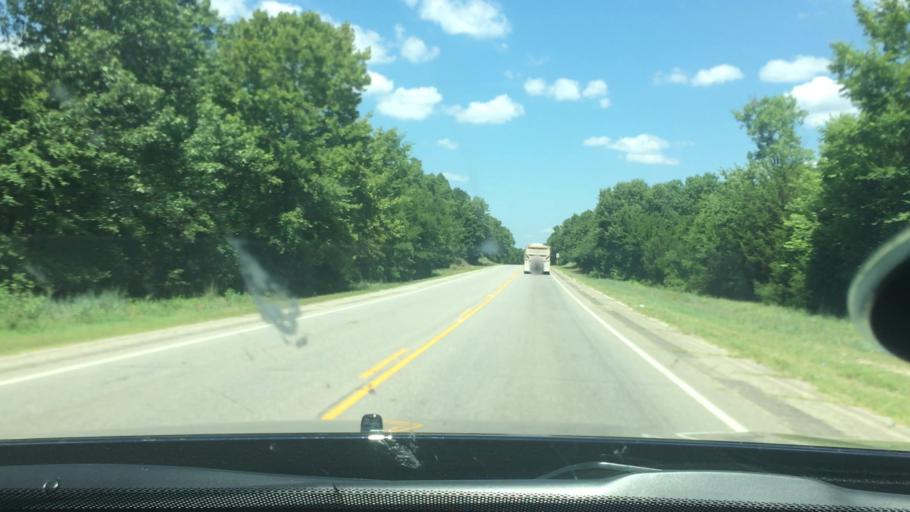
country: US
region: Oklahoma
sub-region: Marshall County
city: Oakland
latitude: 34.1622
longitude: -96.8258
